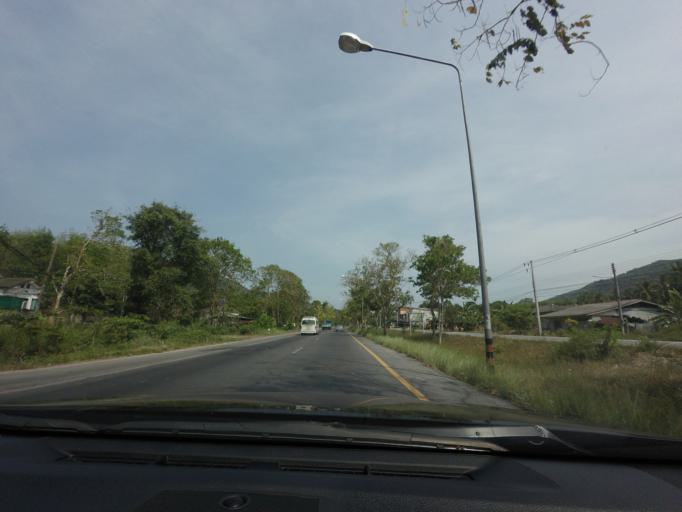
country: TH
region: Pattani
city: Mayo
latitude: 6.7491
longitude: 101.4885
